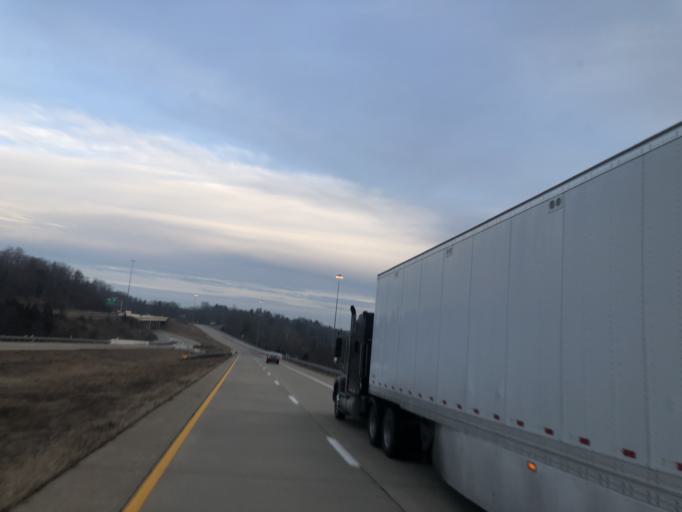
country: US
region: Ohio
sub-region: Athens County
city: Athens
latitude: 39.3019
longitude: -82.1030
